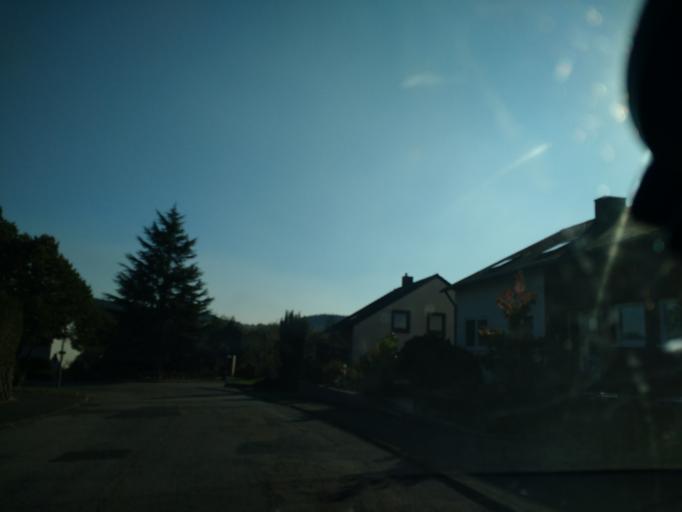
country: DE
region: Rheinland-Pfalz
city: Konz
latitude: 49.6978
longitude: 6.5862
